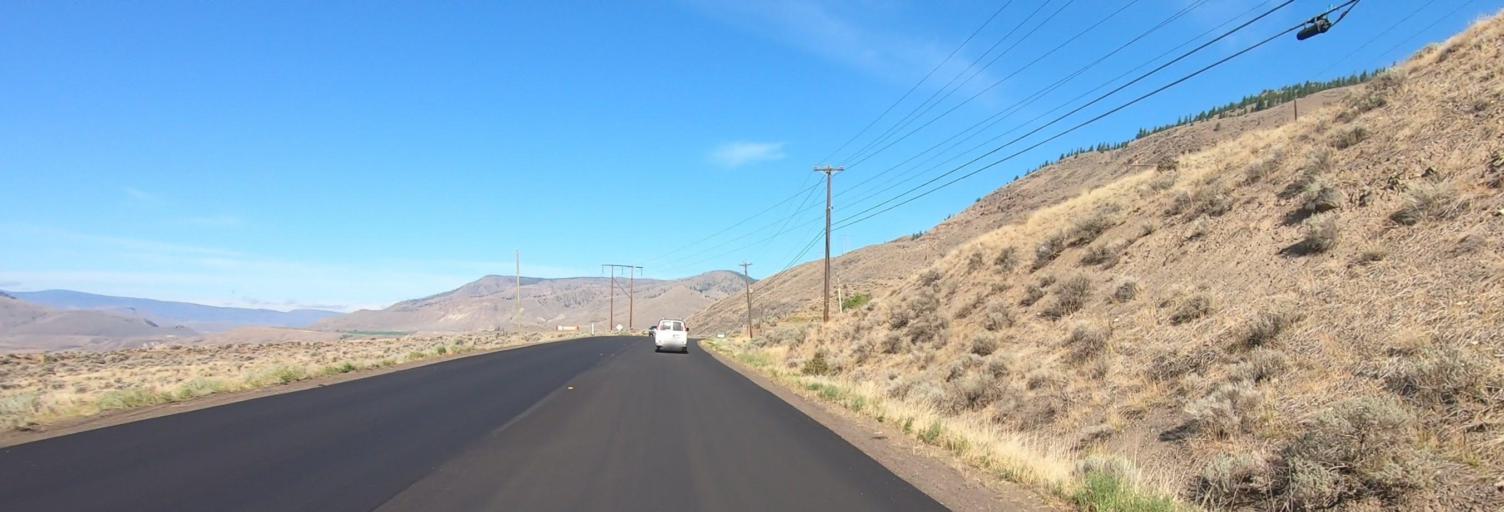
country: CA
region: British Columbia
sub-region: Thompson-Nicola Regional District
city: Ashcroft
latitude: 50.7878
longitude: -121.0713
